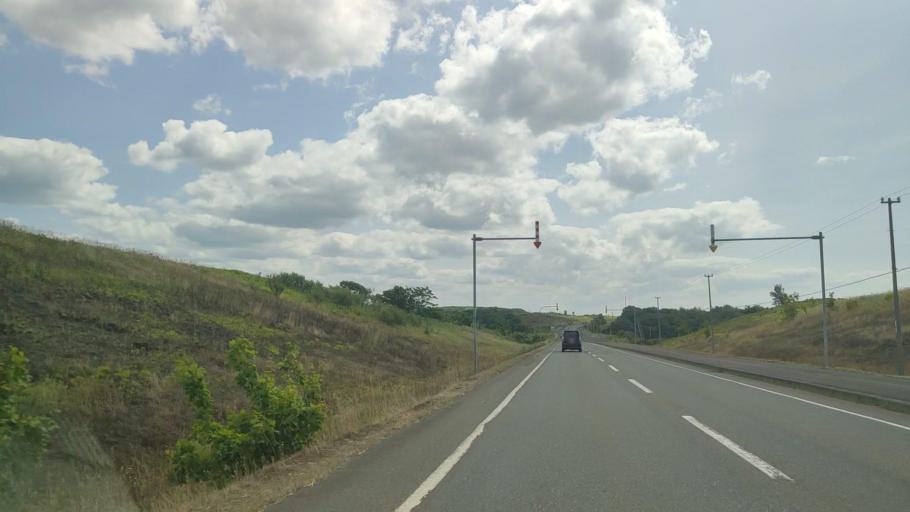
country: JP
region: Hokkaido
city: Makubetsu
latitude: 44.7961
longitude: 141.7888
